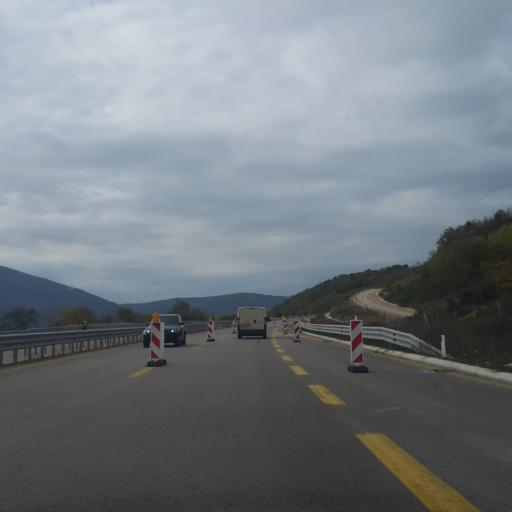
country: RS
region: Central Serbia
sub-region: Pirotski Okrug
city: Bela Palanka
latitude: 43.2351
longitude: 22.3100
